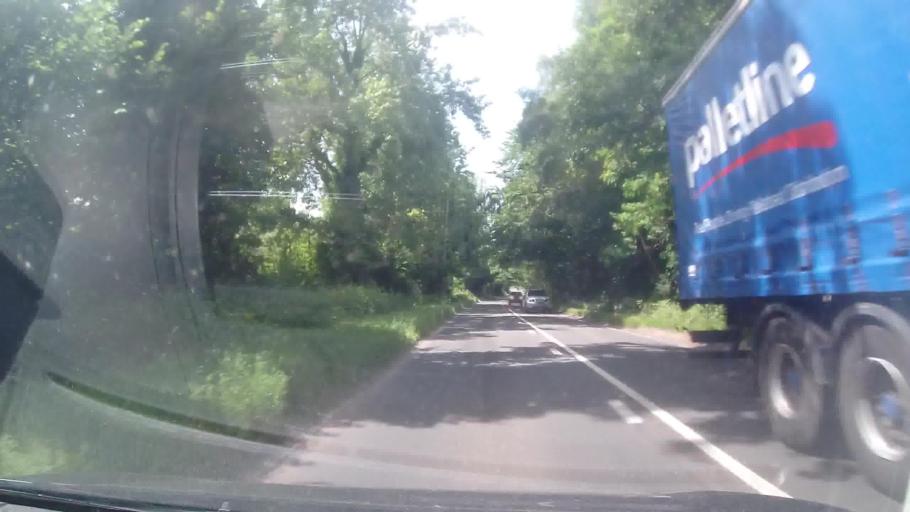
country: GB
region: England
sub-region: Herefordshire
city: Bodenham
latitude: 52.1673
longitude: -2.6801
